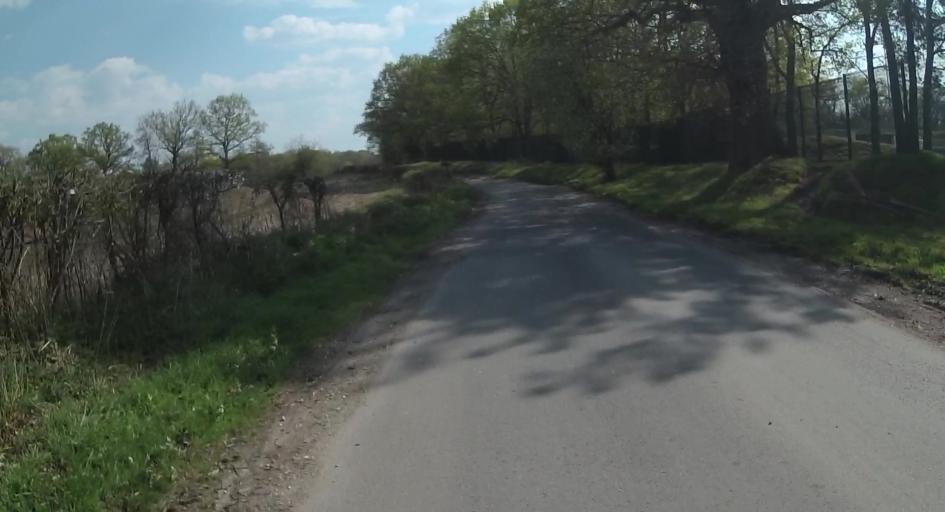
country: GB
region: England
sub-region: Hampshire
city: Tadley
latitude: 51.3895
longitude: -1.1060
